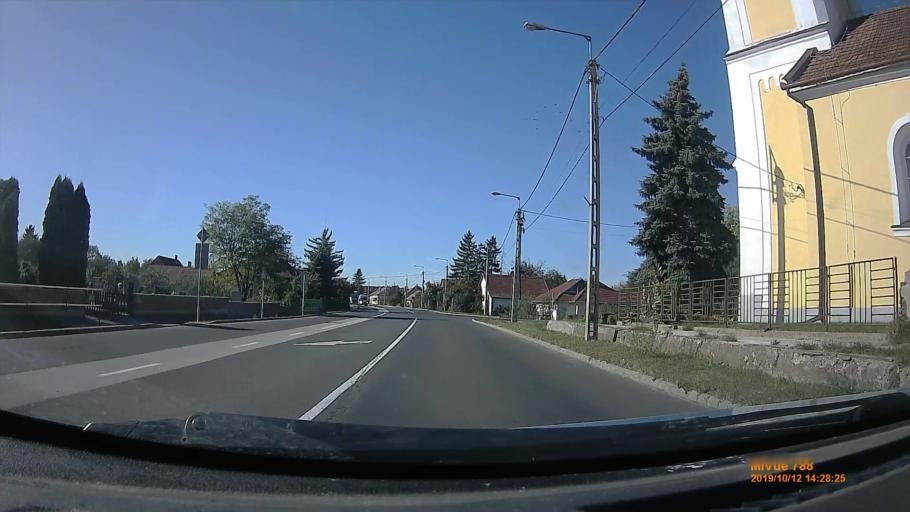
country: HU
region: Hajdu-Bihar
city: Berettyoujfalu
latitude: 47.1673
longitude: 21.6241
